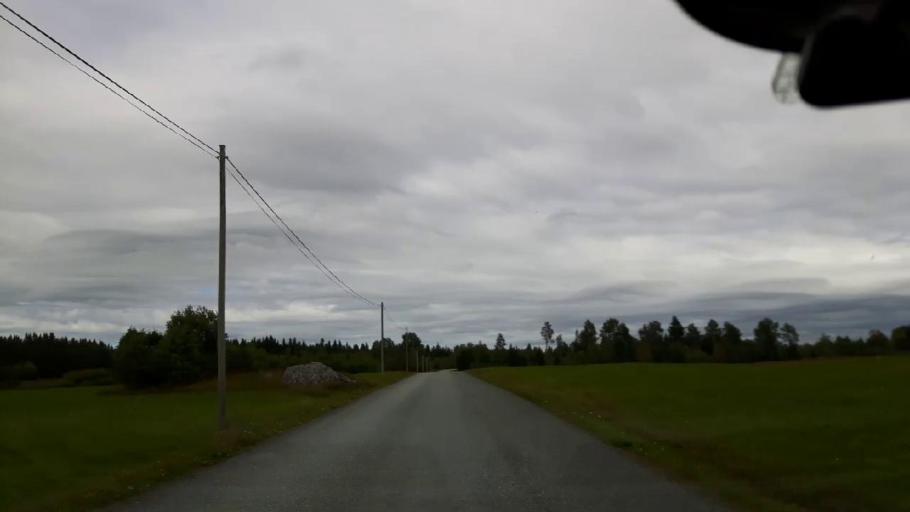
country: SE
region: Jaemtland
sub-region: OEstersunds Kommun
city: Brunflo
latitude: 63.0826
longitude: 14.8727
